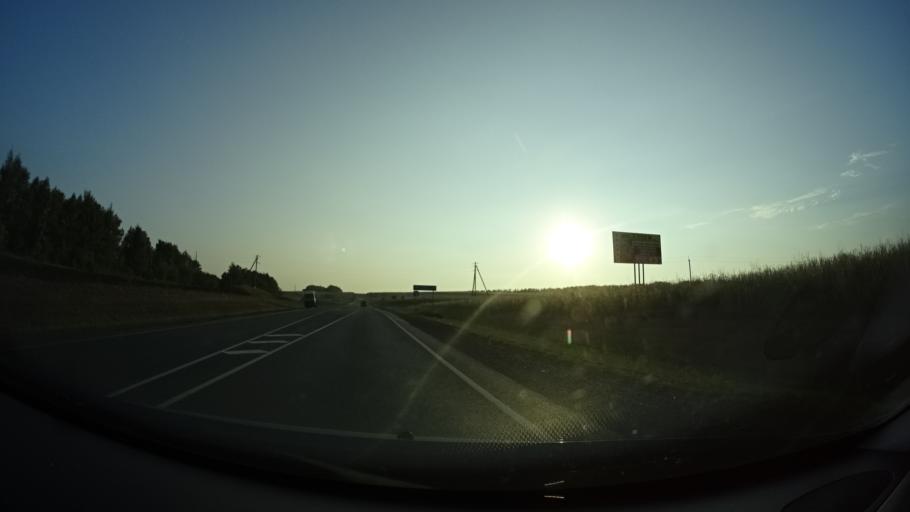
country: RU
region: Samara
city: Klyavlino
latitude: 54.0216
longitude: 51.8303
